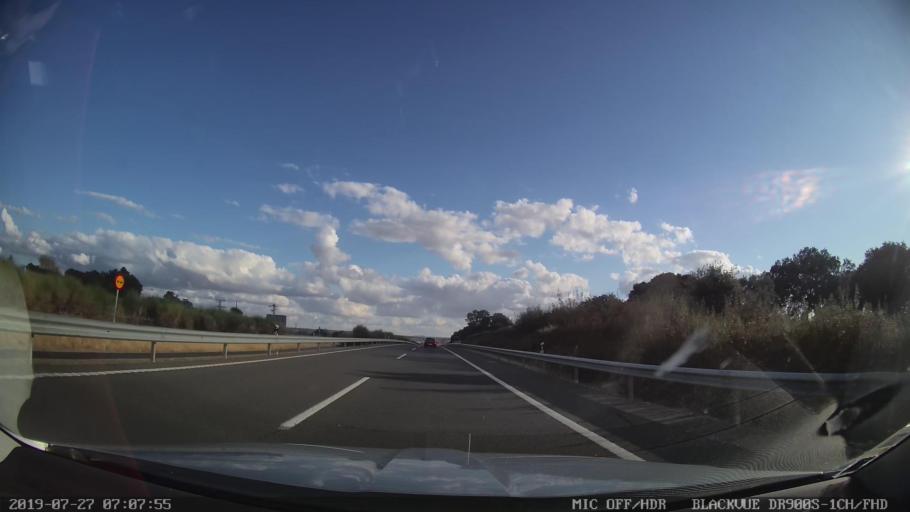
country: ES
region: Extremadura
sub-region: Provincia de Caceres
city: Jaraicejo
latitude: 39.6215
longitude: -5.8268
